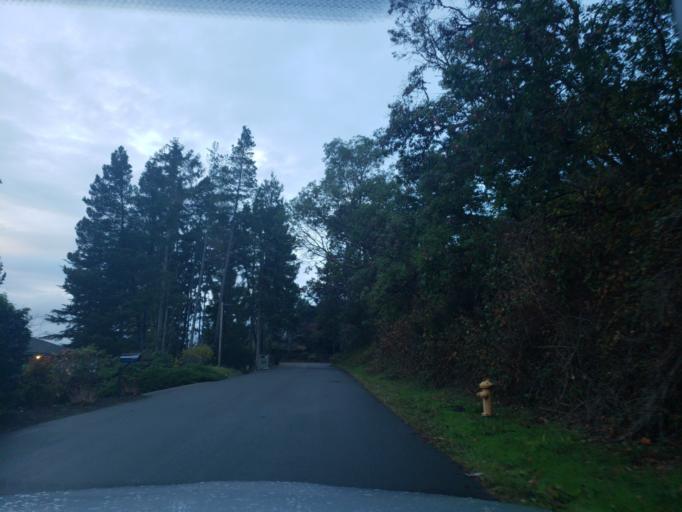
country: US
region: Washington
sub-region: Snohomish County
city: Woodway
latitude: 47.7622
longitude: -122.3817
